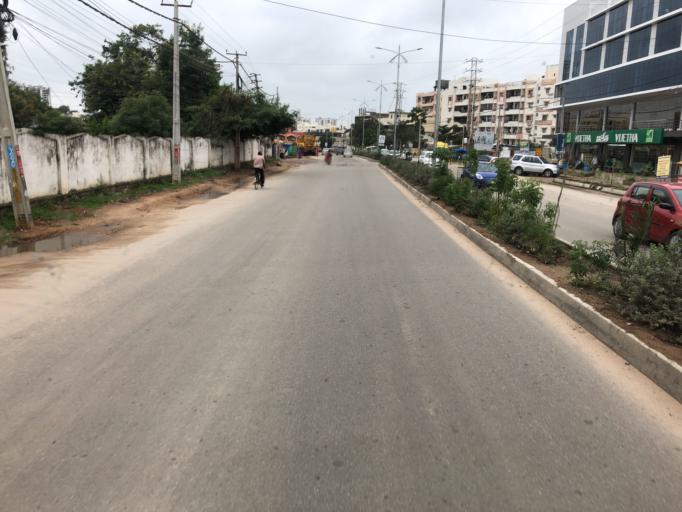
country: IN
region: Telangana
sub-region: Medak
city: Serilingampalle
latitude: 17.4642
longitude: 78.3455
